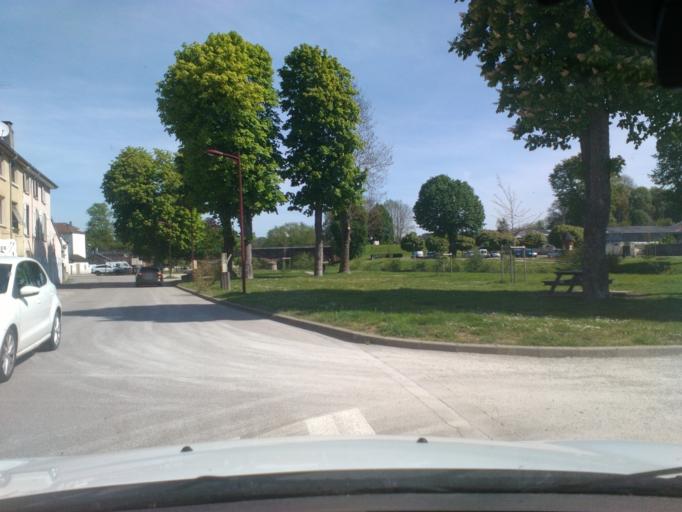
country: FR
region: Lorraine
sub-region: Departement des Vosges
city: Mirecourt
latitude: 48.3016
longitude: 6.1360
